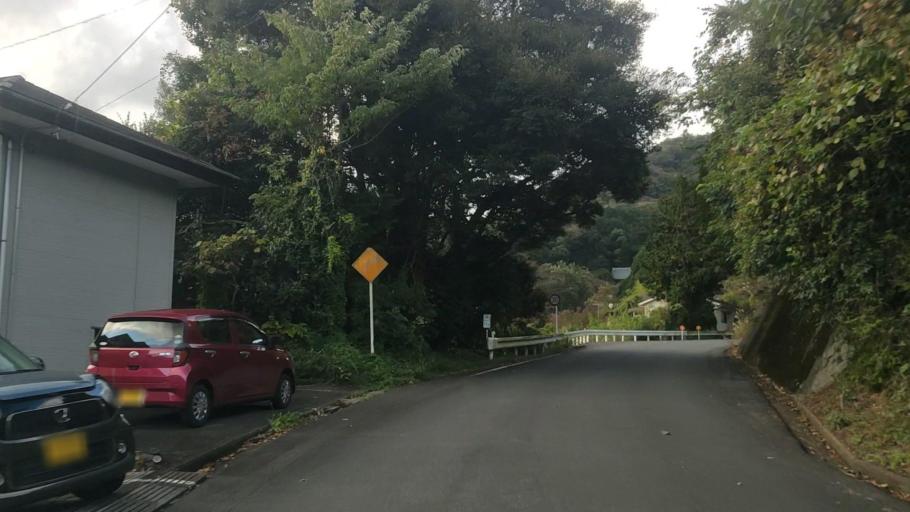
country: JP
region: Shizuoka
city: Ito
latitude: 34.9561
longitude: 139.0764
